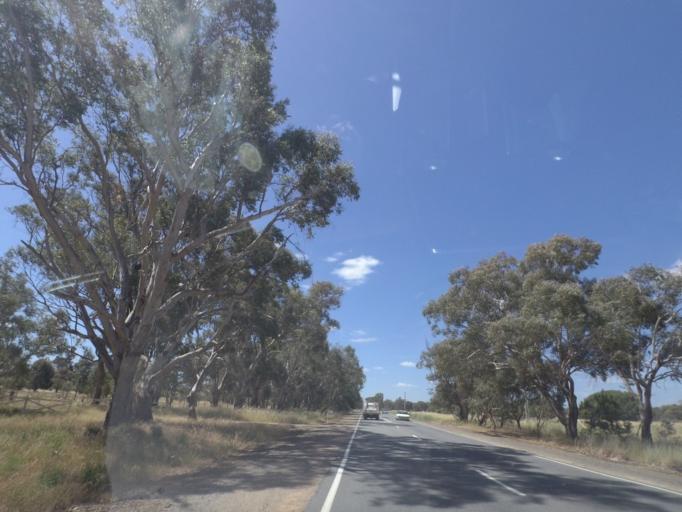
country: AU
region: Victoria
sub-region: Wangaratta
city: Wangaratta
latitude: -36.4141
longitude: 146.2665
